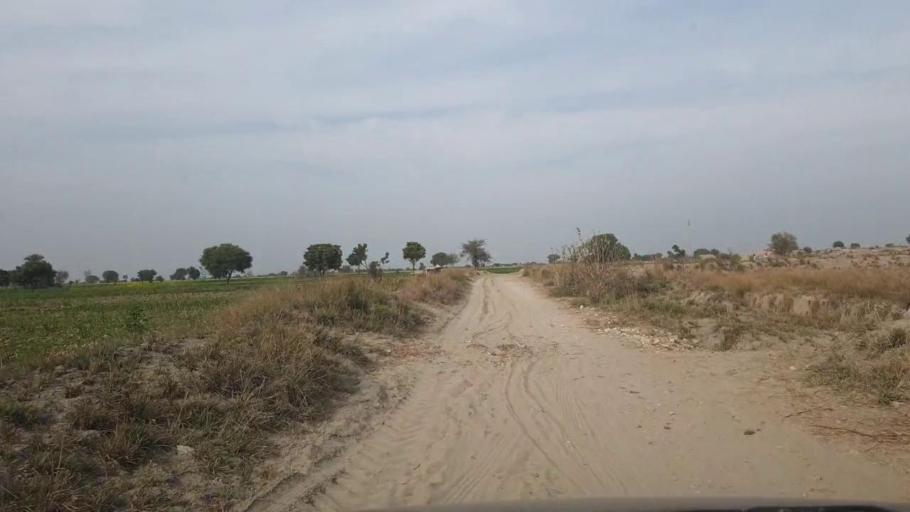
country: PK
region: Sindh
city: Shahpur Chakar
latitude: 26.1159
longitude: 68.5082
